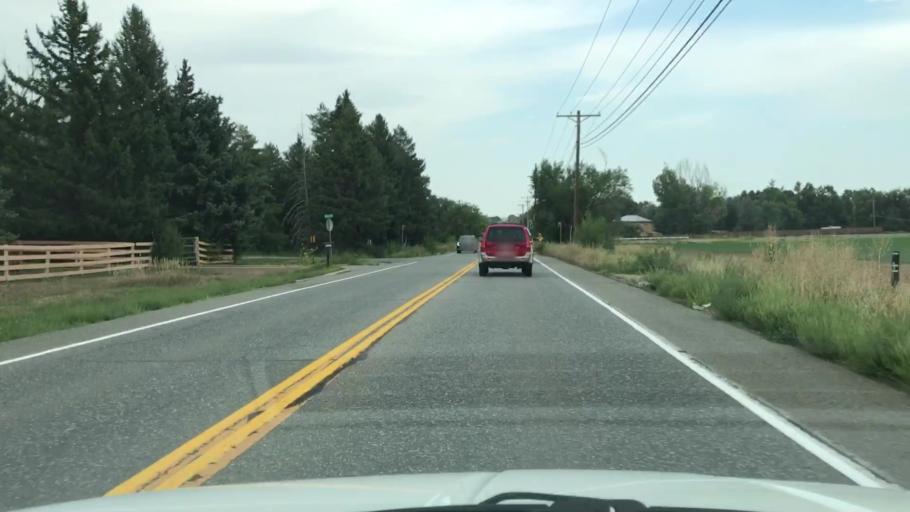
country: US
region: Colorado
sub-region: Boulder County
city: Louisville
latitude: 40.0001
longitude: -105.1443
